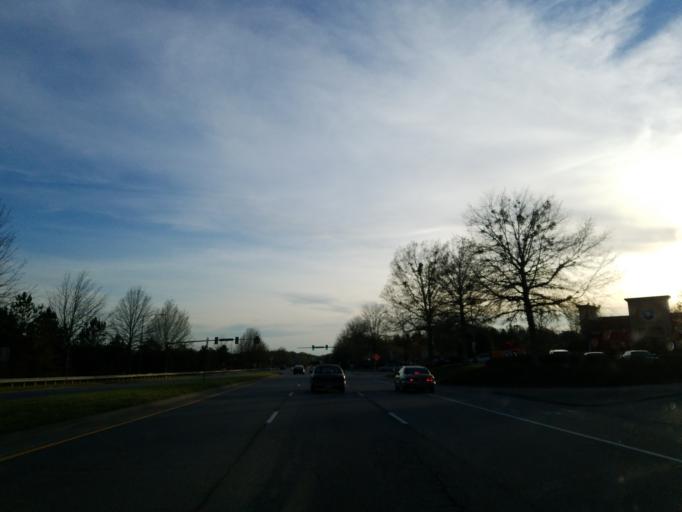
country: US
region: Georgia
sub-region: Cherokee County
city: Canton
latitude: 34.2496
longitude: -84.4762
